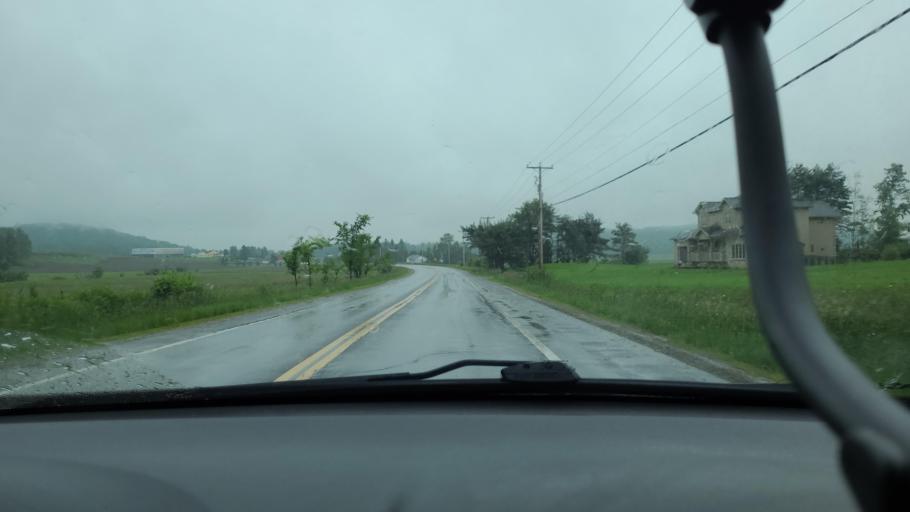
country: CA
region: Quebec
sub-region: Outaouais
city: Saint-Andre-Avellin
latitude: 45.7011
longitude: -75.0515
